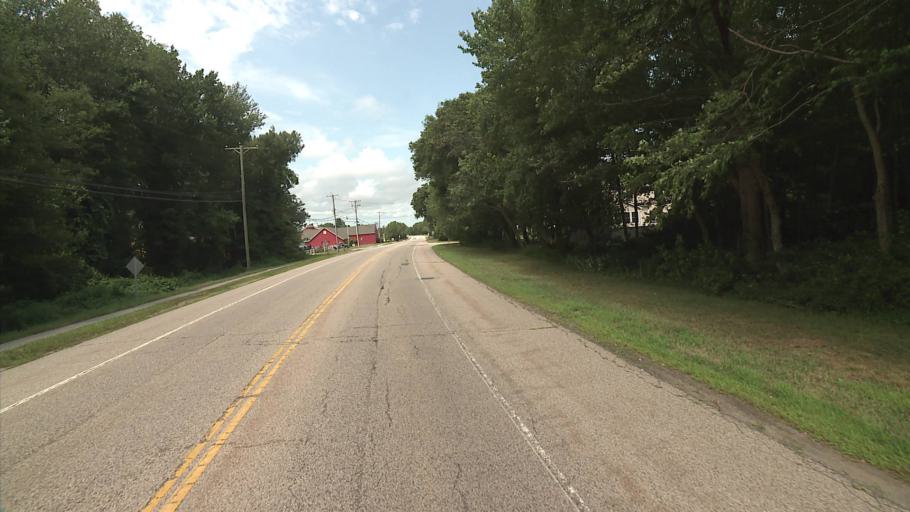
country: US
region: Connecticut
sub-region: New London County
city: Central Waterford
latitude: 41.3310
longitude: -72.1356
